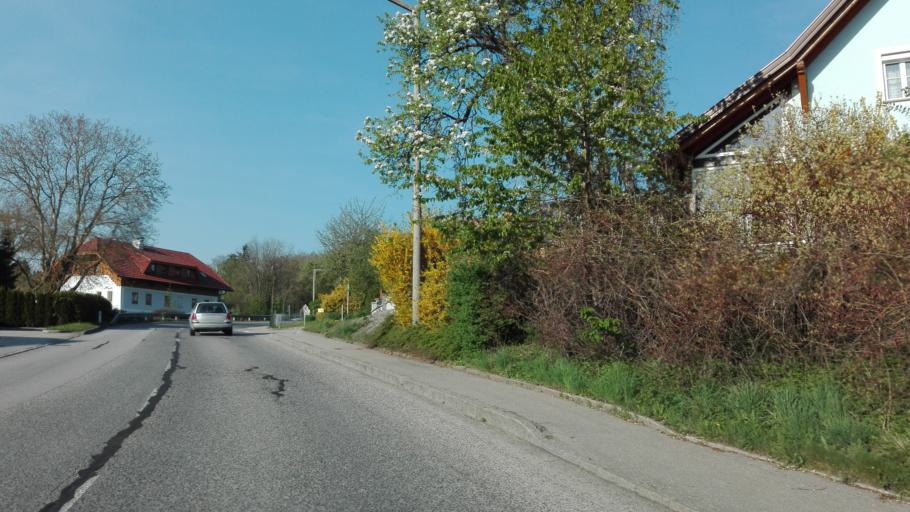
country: AT
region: Upper Austria
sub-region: Politischer Bezirk Grieskirchen
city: Grieskirchen
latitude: 48.3435
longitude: 13.7759
